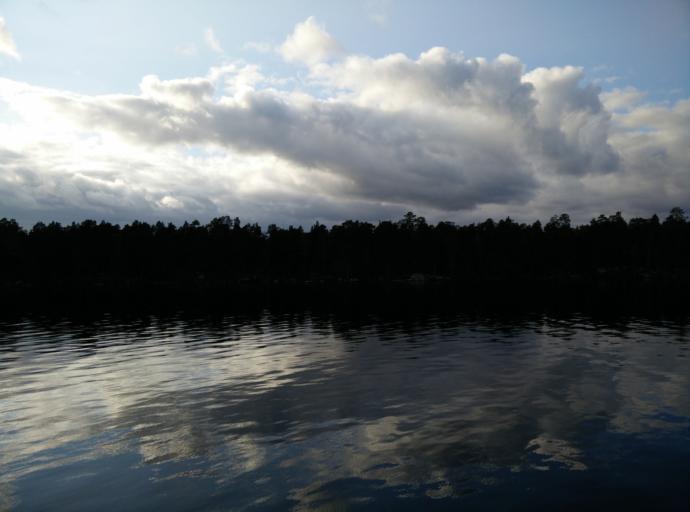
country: FI
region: Lapland
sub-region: Pohjois-Lappi
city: Inari
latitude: 68.9235
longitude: 27.1687
